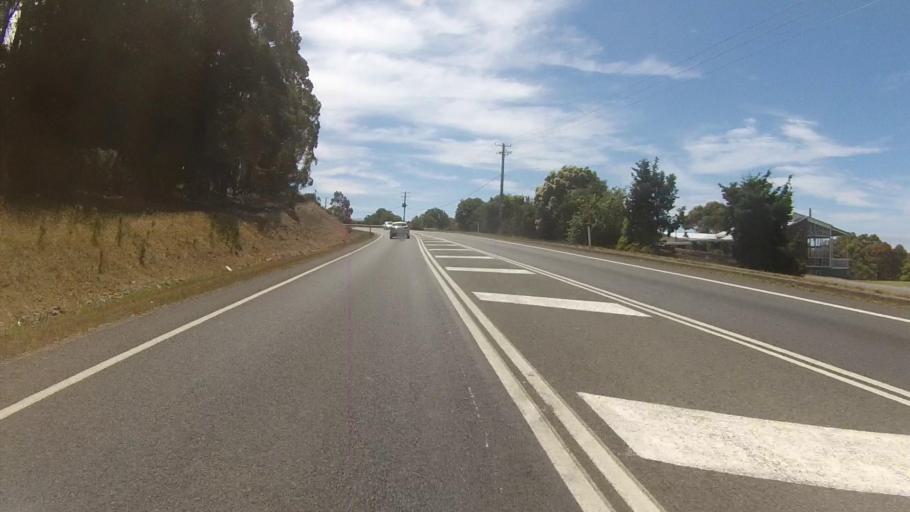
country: AU
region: Tasmania
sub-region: Kingborough
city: Margate
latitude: -43.0046
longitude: 147.2747
